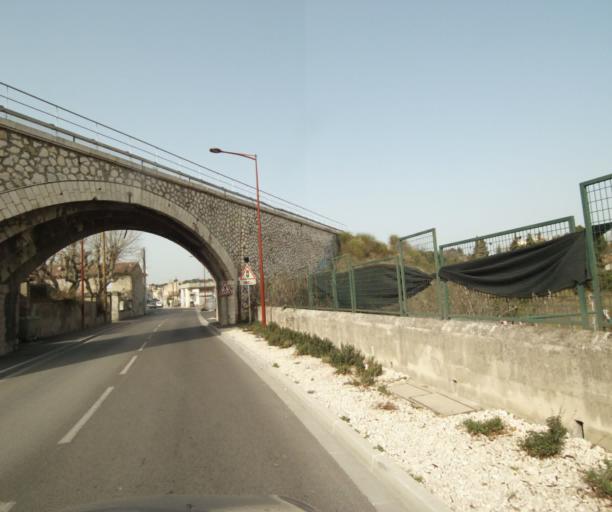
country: FR
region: Provence-Alpes-Cote d'Azur
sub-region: Departement des Bouches-du-Rhone
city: Marseille 15
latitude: 43.3762
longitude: 5.3535
